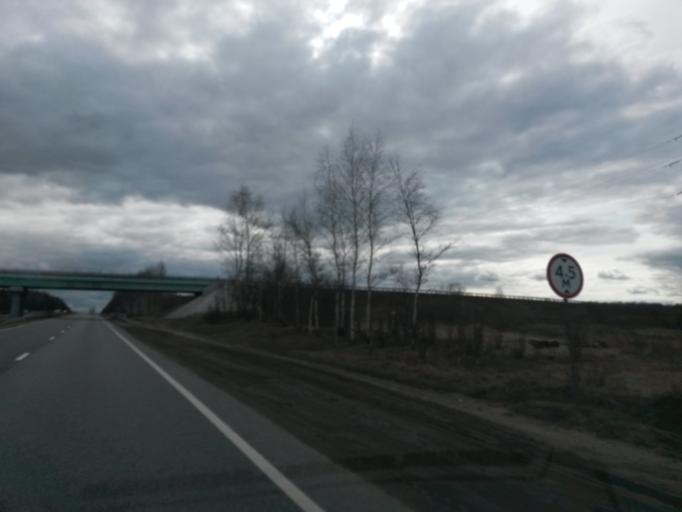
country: RU
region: Jaroslavl
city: Krasnyye Tkachi
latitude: 57.4389
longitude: 39.7082
